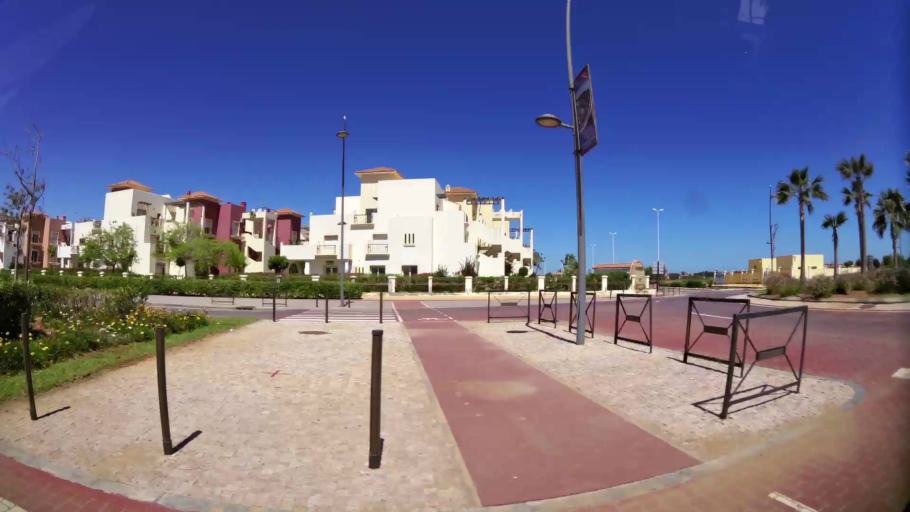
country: MA
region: Oriental
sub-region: Berkane-Taourirt
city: Madagh
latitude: 35.0994
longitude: -2.2999
